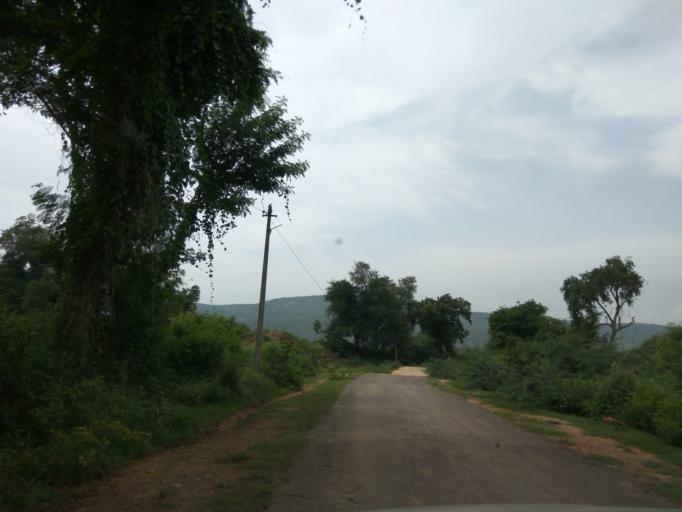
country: IN
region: Andhra Pradesh
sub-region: Prakasam
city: Cumbum
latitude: 15.4512
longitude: 79.0768
